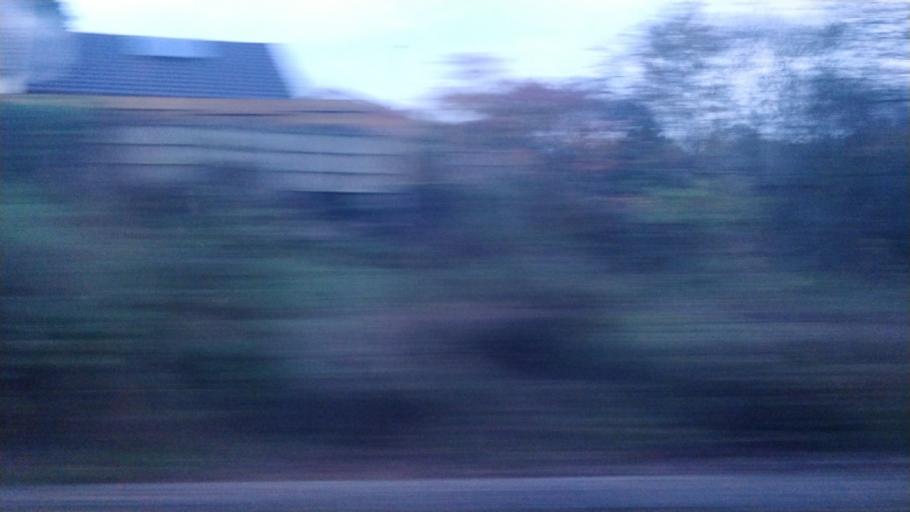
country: GB
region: England
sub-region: Borough of Bolton
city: Westhoughton
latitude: 53.5431
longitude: -2.5389
